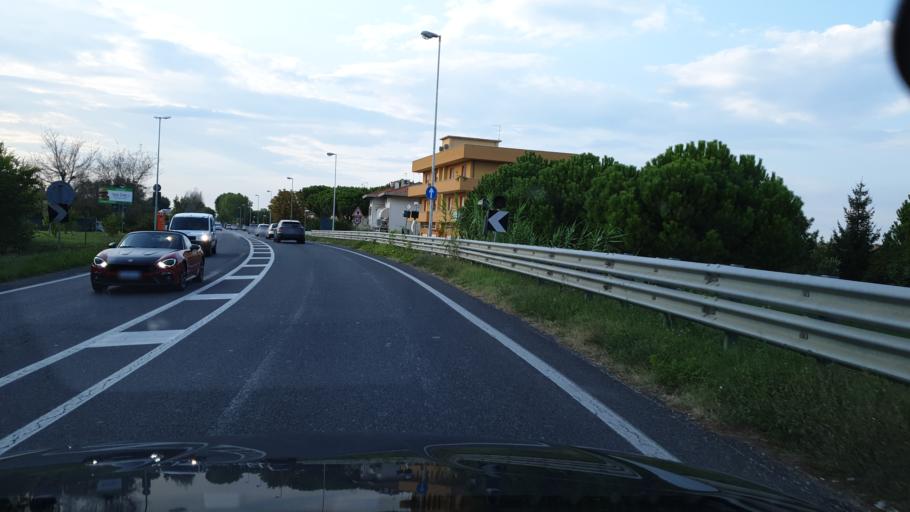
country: IT
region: Emilia-Romagna
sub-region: Provincia di Rimini
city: Riccione
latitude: 44.0159
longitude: 12.6318
